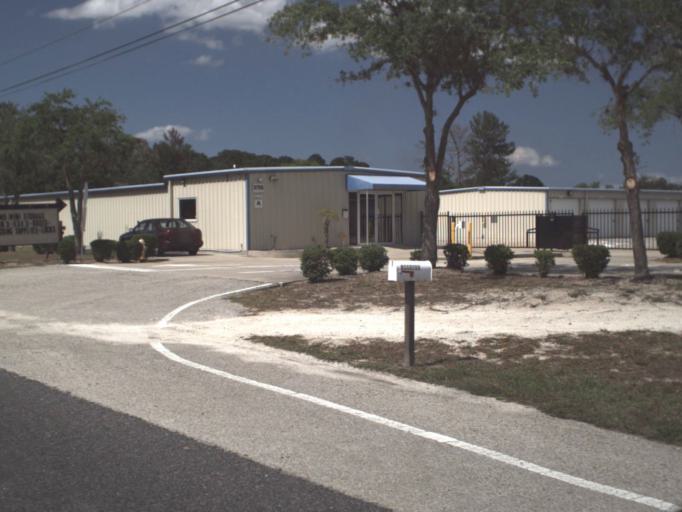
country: US
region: Florida
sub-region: Brevard County
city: Mims
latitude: 28.7013
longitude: -80.8598
